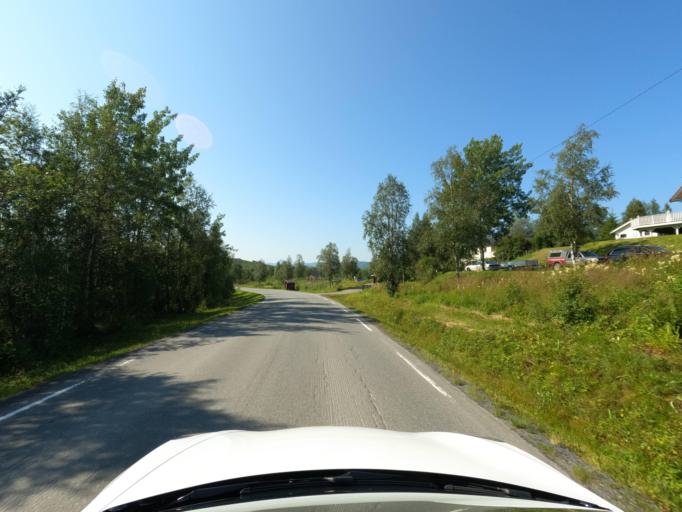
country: NO
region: Nordland
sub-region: Ballangen
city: Ballangen
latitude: 68.3574
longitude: 16.8721
